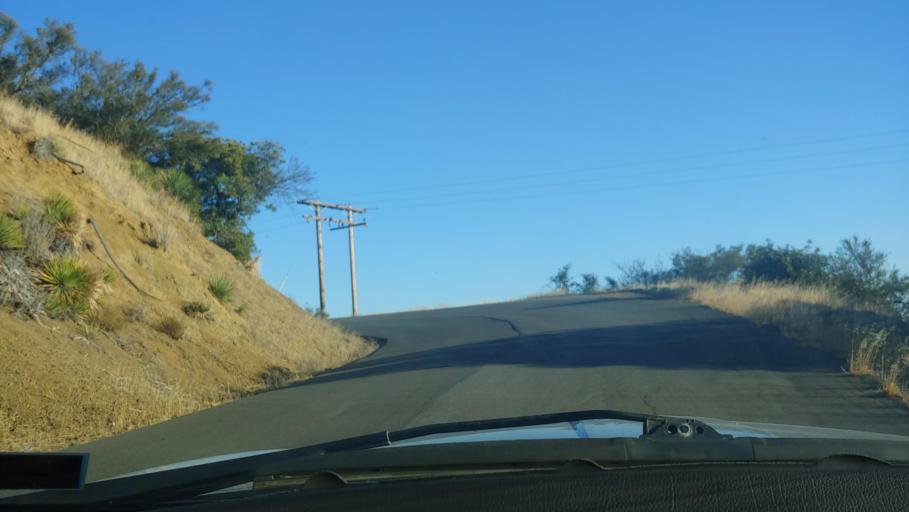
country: US
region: California
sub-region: Santa Barbara County
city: Goleta
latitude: 34.5189
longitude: -119.7921
